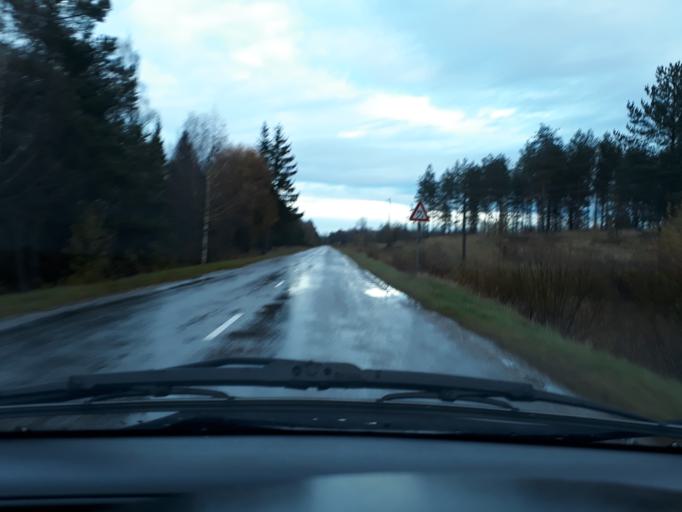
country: LV
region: Dobeles Rajons
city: Dobele
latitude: 56.6049
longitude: 23.2105
